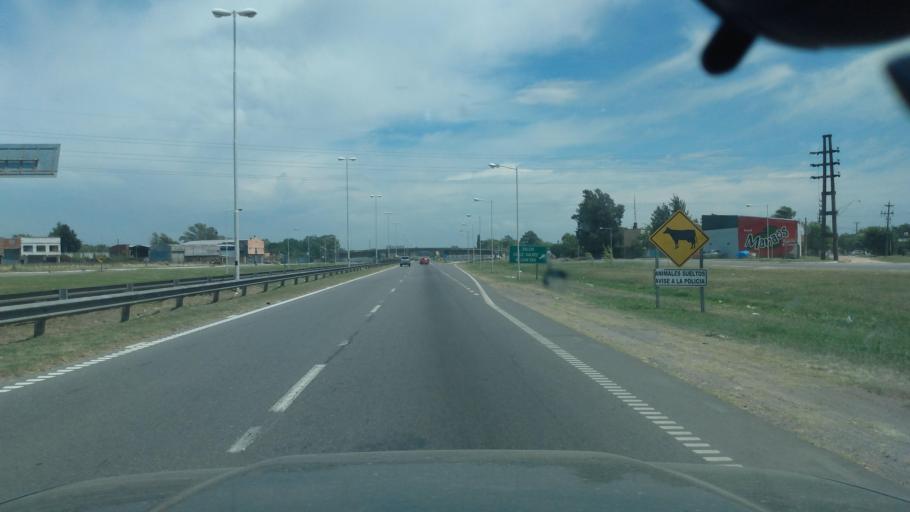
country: AR
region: Buenos Aires
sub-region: Partido de Lujan
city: Lujan
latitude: -34.5540
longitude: -59.1042
